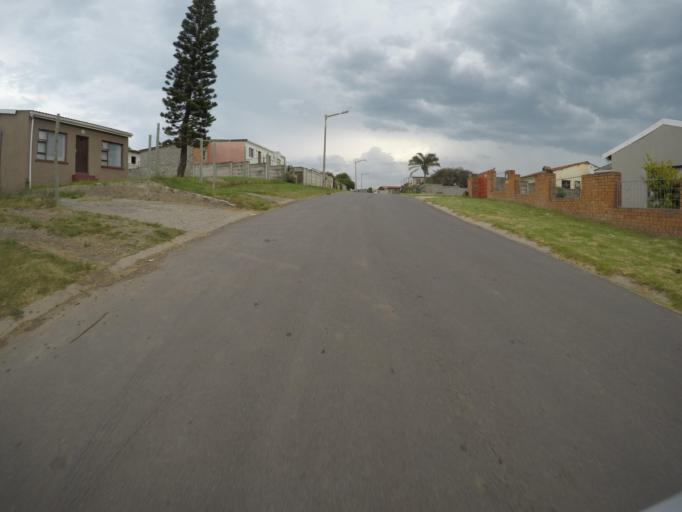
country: ZA
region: Eastern Cape
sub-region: Buffalo City Metropolitan Municipality
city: East London
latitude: -33.0197
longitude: 27.8689
